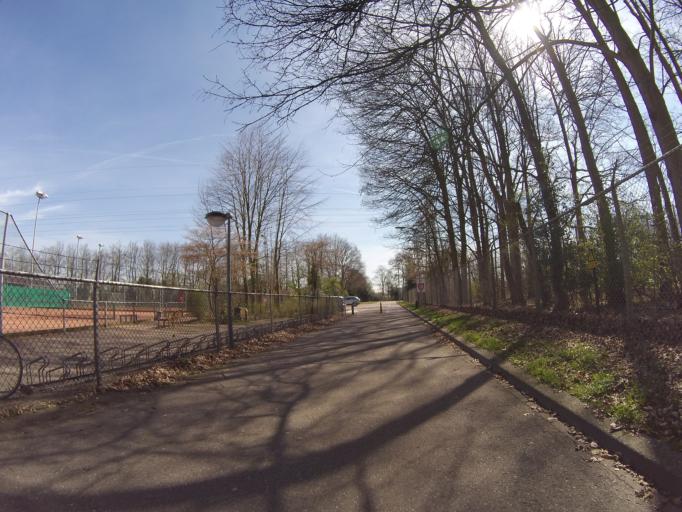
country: NL
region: Gelderland
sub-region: Gemeente Nijkerk
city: Nijkerk
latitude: 52.2264
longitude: 5.5015
